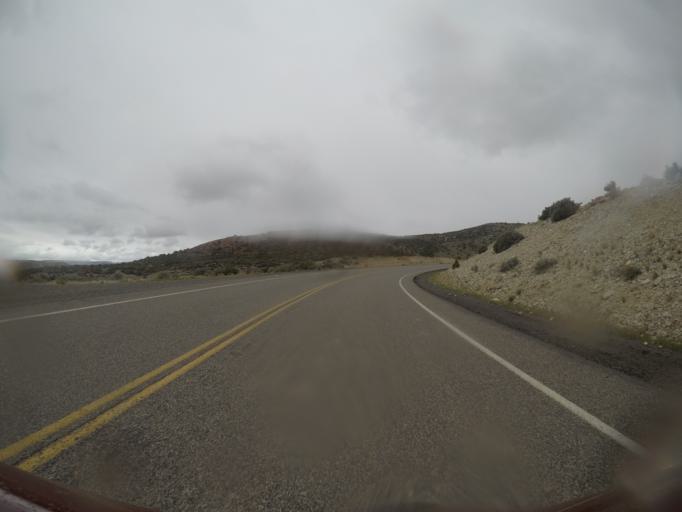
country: US
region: Wyoming
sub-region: Big Horn County
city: Lovell
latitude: 45.0310
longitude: -108.2620
